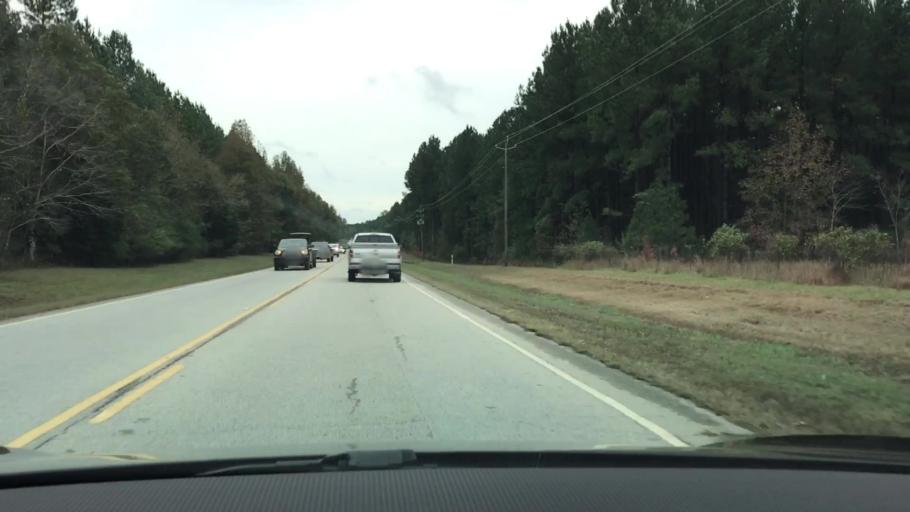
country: US
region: Georgia
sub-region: Warren County
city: Firing Range
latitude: 33.4484
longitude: -82.6951
